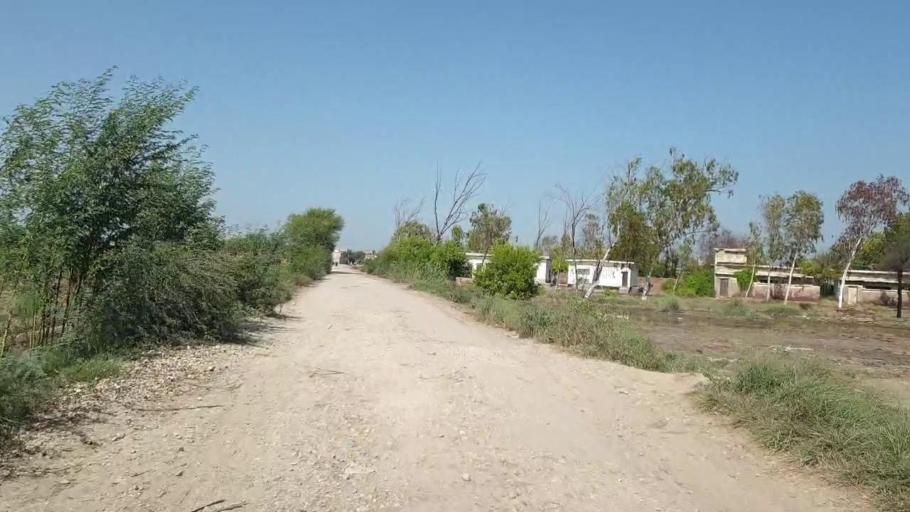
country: PK
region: Sindh
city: Matiari
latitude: 25.4974
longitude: 68.4637
